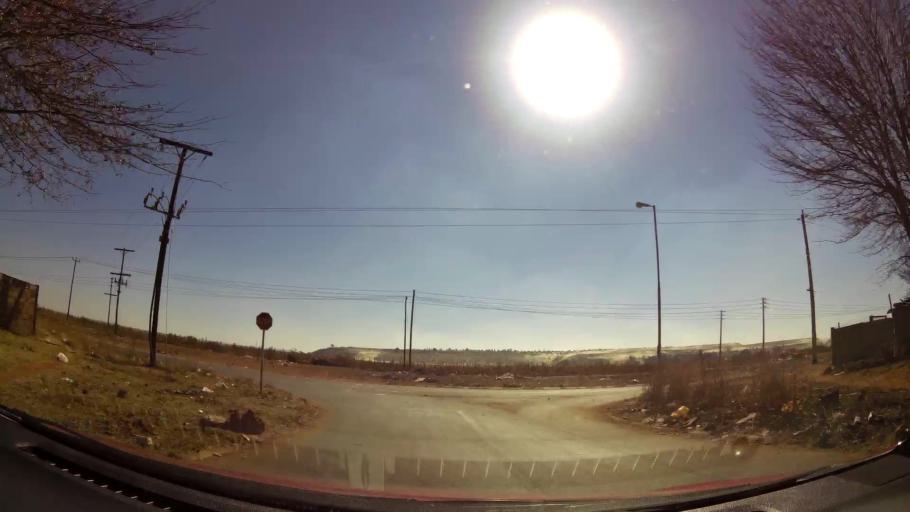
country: ZA
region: Gauteng
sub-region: City of Johannesburg Metropolitan Municipality
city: Soweto
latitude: -26.2157
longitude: 27.8326
